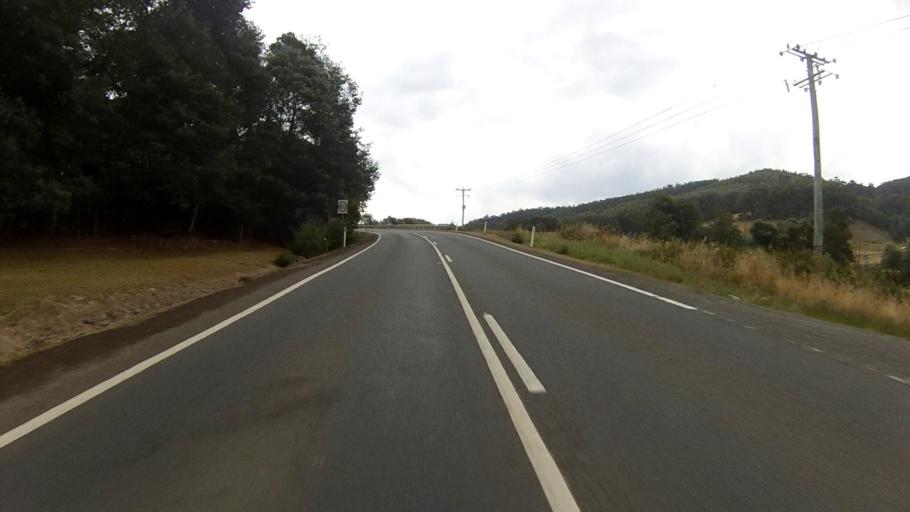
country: AU
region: Tasmania
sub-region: Huon Valley
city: Cygnet
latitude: -43.1357
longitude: 147.0541
